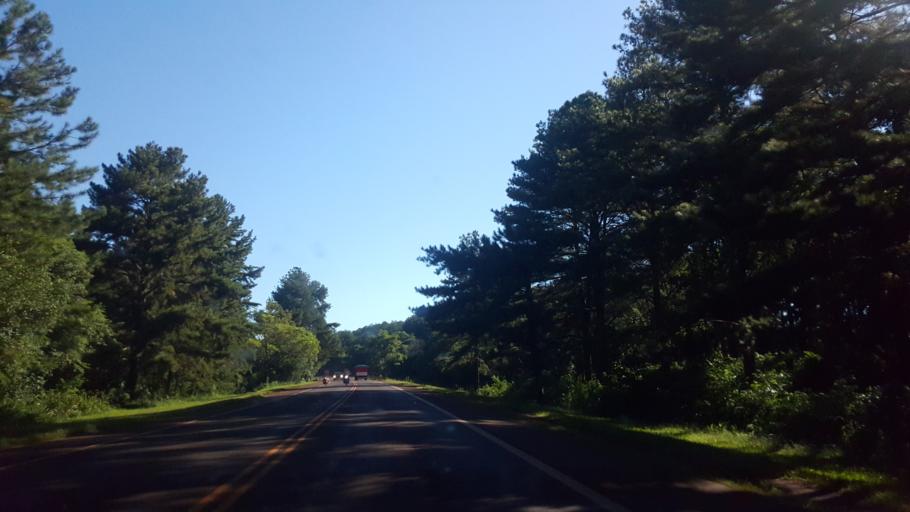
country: AR
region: Misiones
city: Puerto Libertad
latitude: -25.9061
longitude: -54.5667
